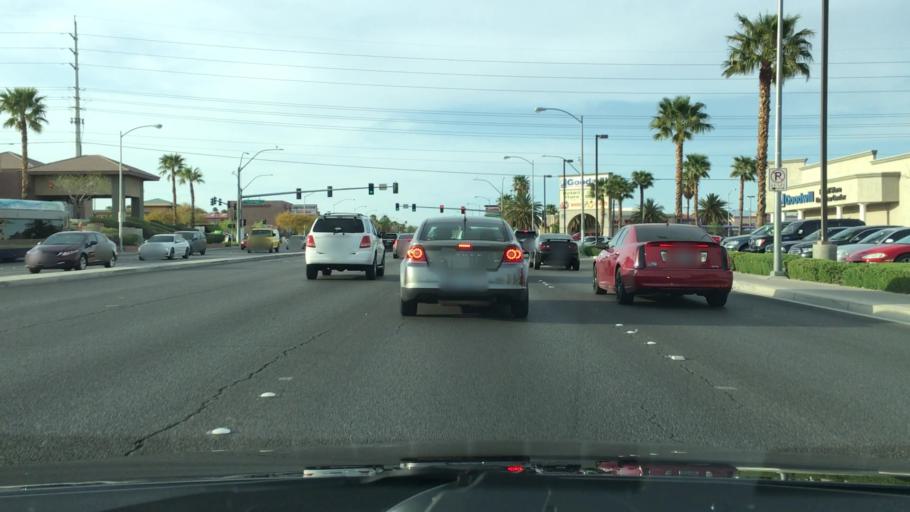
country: US
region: Nevada
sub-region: Clark County
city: Summerlin South
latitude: 36.1138
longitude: -115.2970
